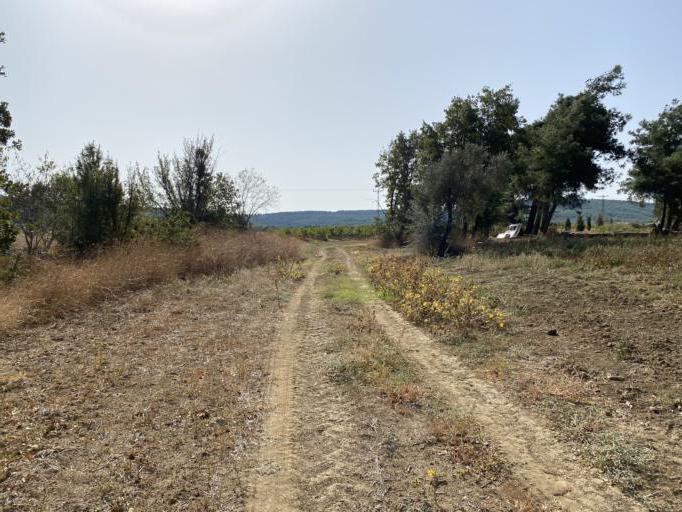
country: TR
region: Canakkale
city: Eceabat
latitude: 40.1814
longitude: 26.2875
